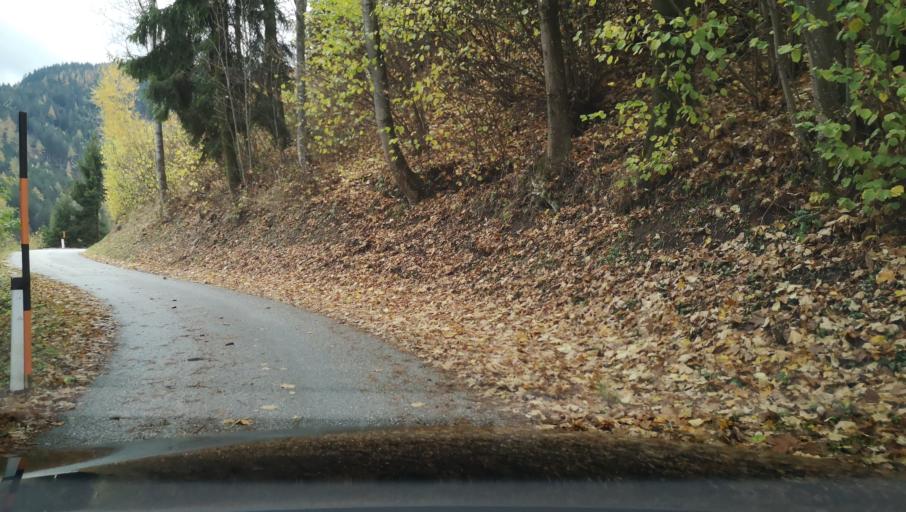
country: AT
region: Styria
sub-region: Politischer Bezirk Weiz
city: Birkfeld
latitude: 47.3681
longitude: 15.6362
